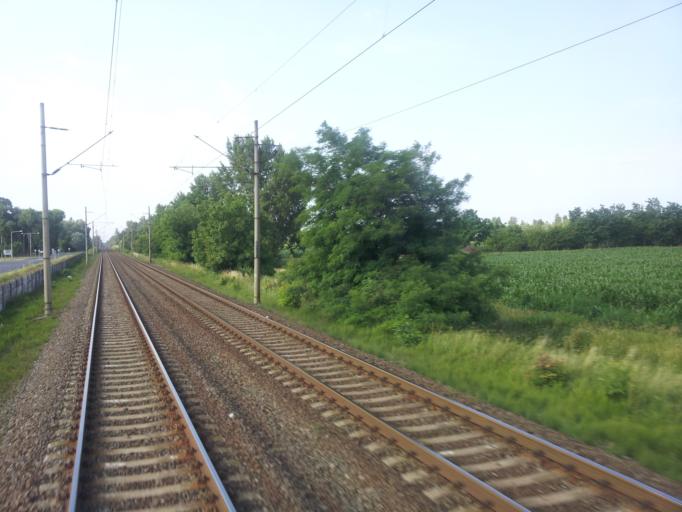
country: HU
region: Fejer
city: Szekesfehervar
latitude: 47.1466
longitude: 18.4078
